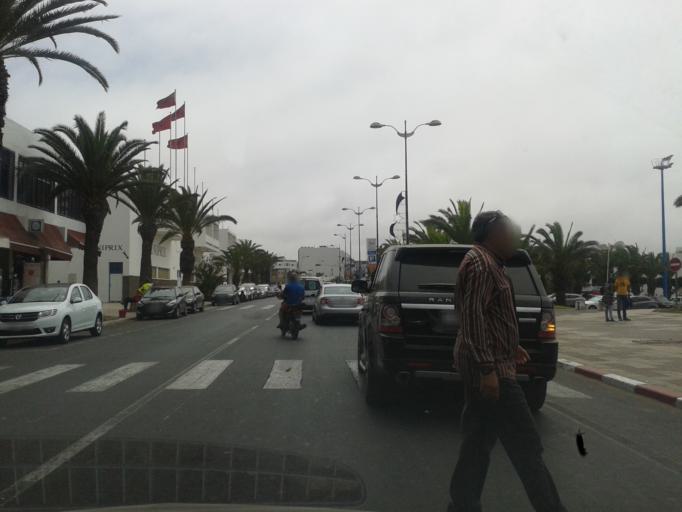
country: MA
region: Souss-Massa-Draa
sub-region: Agadir-Ida-ou-Tnan
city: Agadir
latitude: 30.4211
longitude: -9.6001
